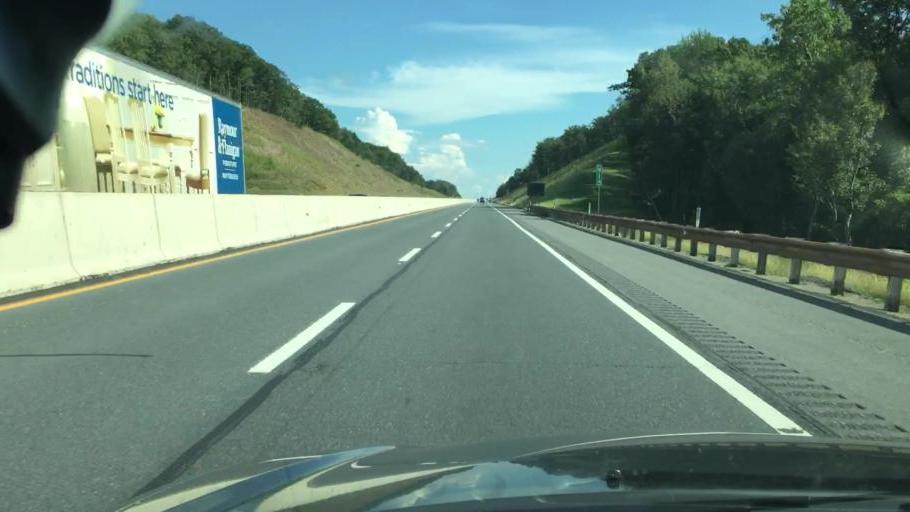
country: US
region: Pennsylvania
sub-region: Carbon County
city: Towamensing Trails
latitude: 41.0407
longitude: -75.6646
